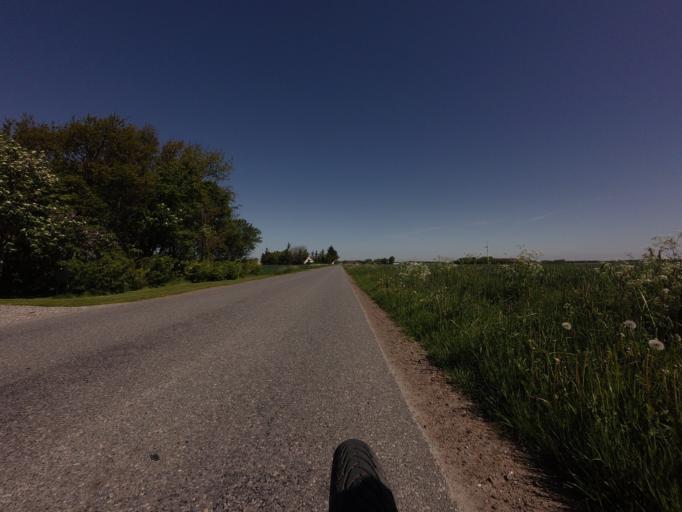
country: DK
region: North Denmark
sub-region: Hjorring Kommune
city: Vra
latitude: 57.3952
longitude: 9.8713
